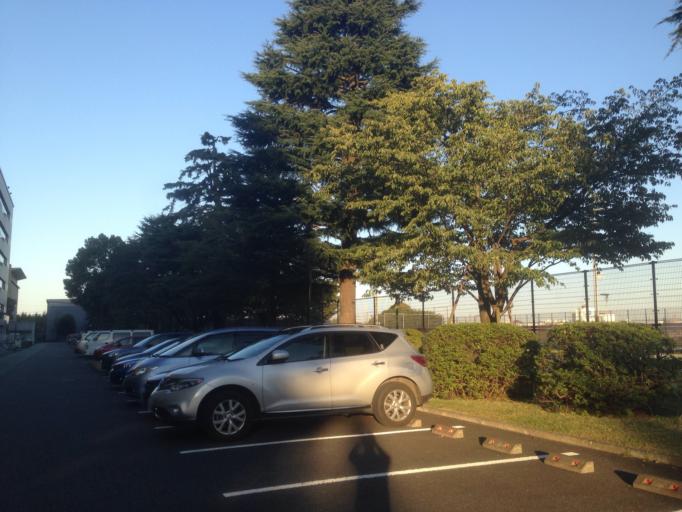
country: JP
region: Tokyo
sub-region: Machida-shi
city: Machida
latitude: 35.5651
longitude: 139.4028
